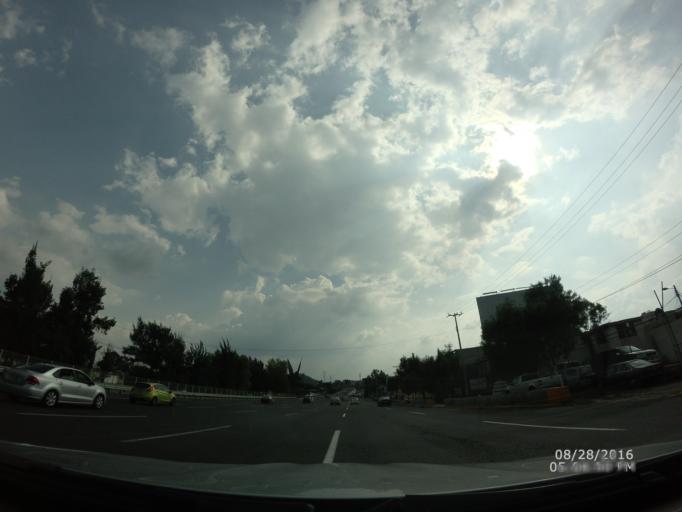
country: MX
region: Mexico
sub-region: Tlalnepantla de Baz
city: Puerto Escondido (Tepeolulco Puerto Escondido)
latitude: 19.5242
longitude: -99.0890
